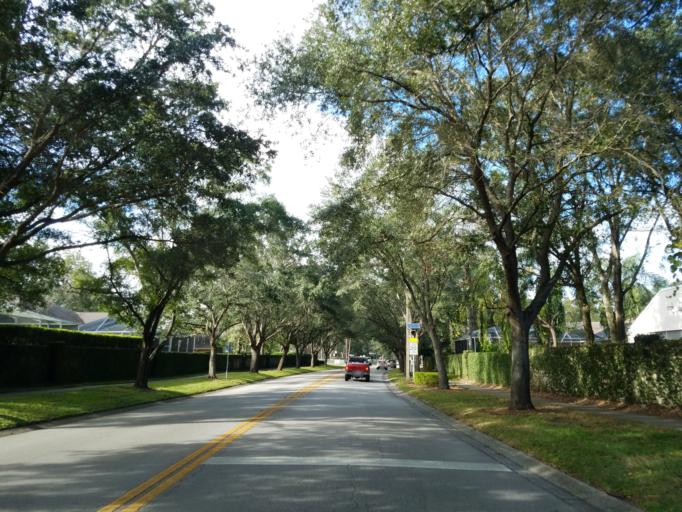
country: US
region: Florida
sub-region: Hillsborough County
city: Bloomingdale
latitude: 27.8856
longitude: -82.2469
